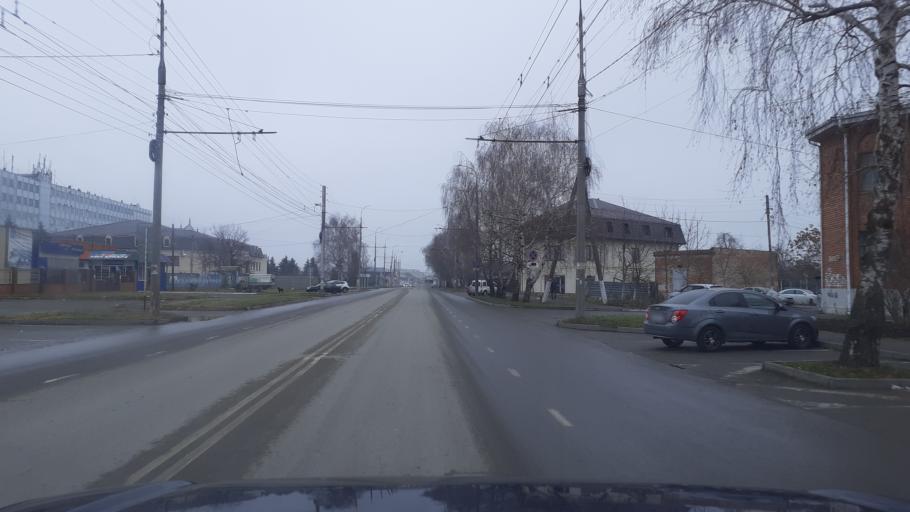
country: RU
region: Adygeya
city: Maykop
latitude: 44.6232
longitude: 40.0695
